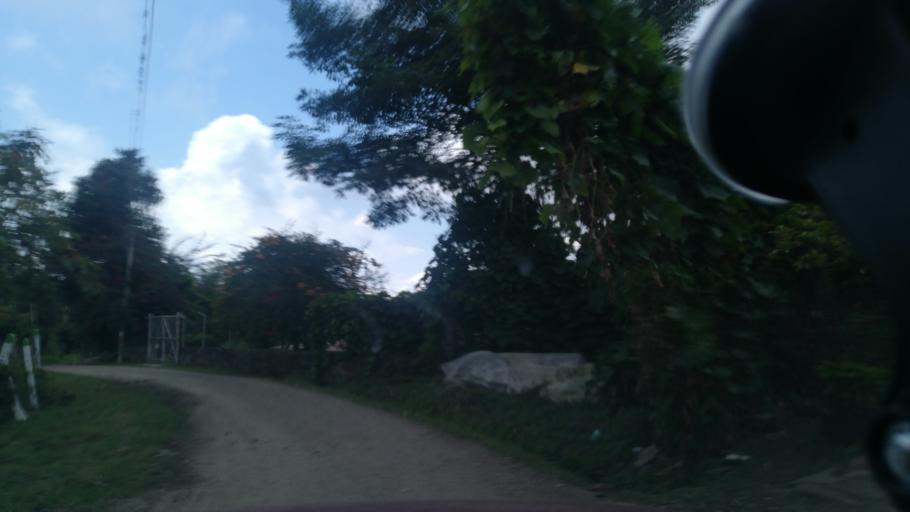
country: CO
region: Cundinamarca
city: San Antonio del Tequendama
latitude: 4.6582
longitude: -74.3952
